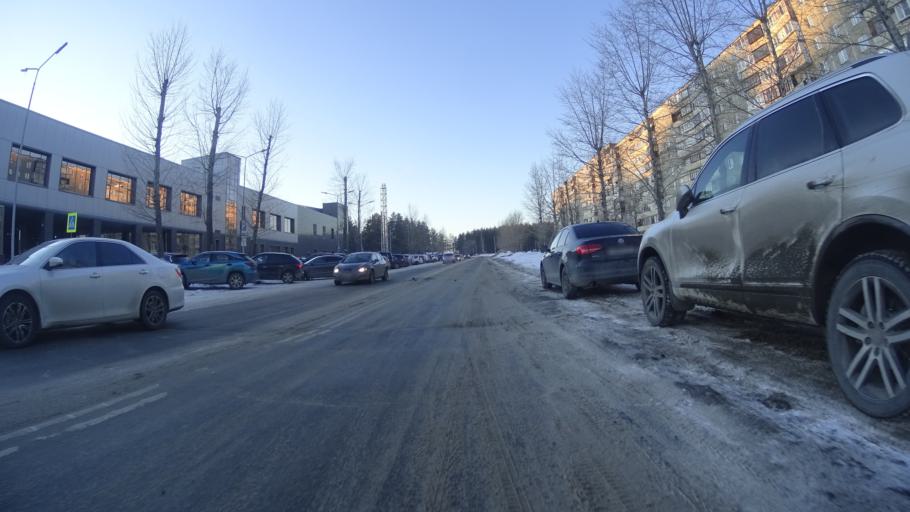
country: RU
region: Chelyabinsk
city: Roshchino
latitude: 55.1950
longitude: 61.2998
